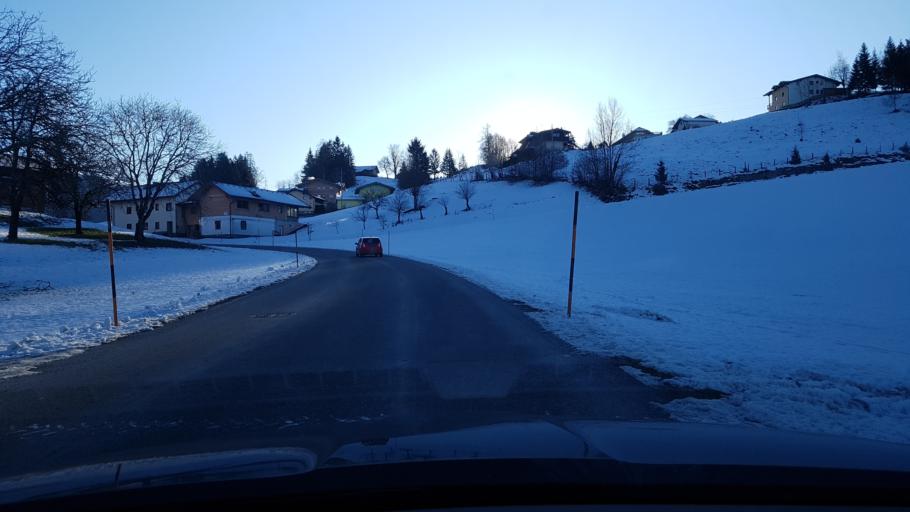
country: AT
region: Salzburg
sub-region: Politischer Bezirk Hallein
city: Kuchl
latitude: 47.6573
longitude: 13.1895
